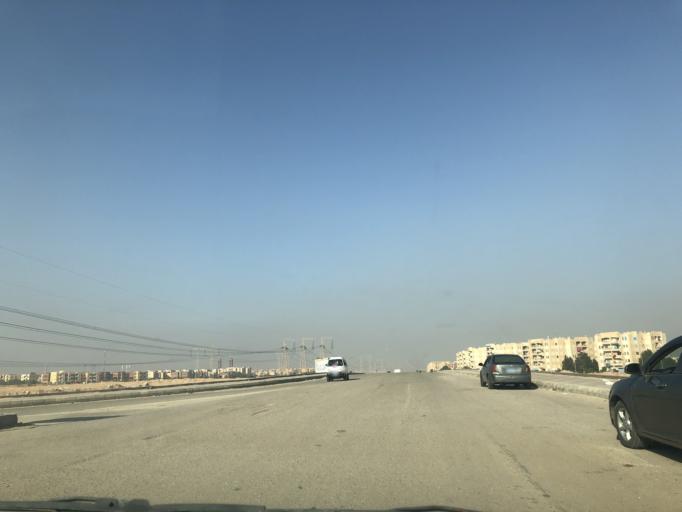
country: EG
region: Al Jizah
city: Madinat Sittah Uktubar
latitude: 29.9218
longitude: 31.0547
